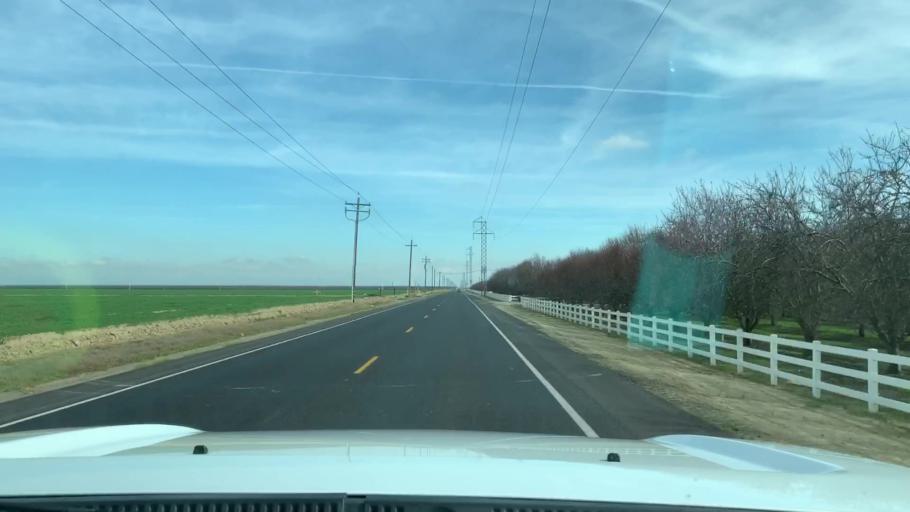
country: US
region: California
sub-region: Kern County
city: Shafter
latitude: 35.4420
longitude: -119.3475
